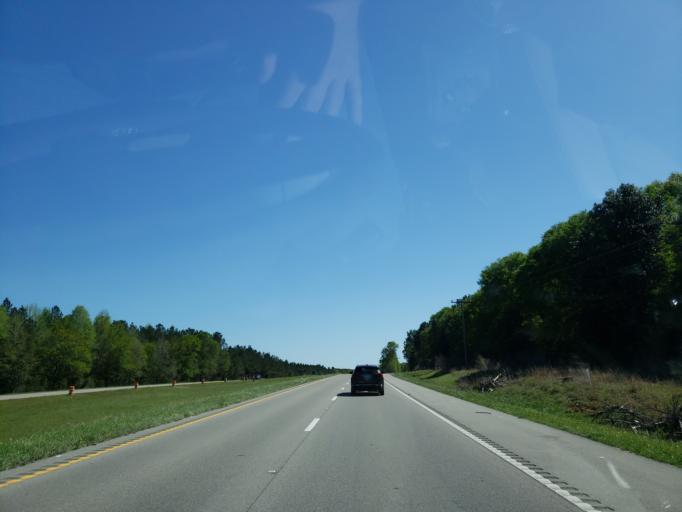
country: US
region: Mississippi
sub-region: Stone County
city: Wiggins
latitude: 31.0028
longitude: -89.2017
